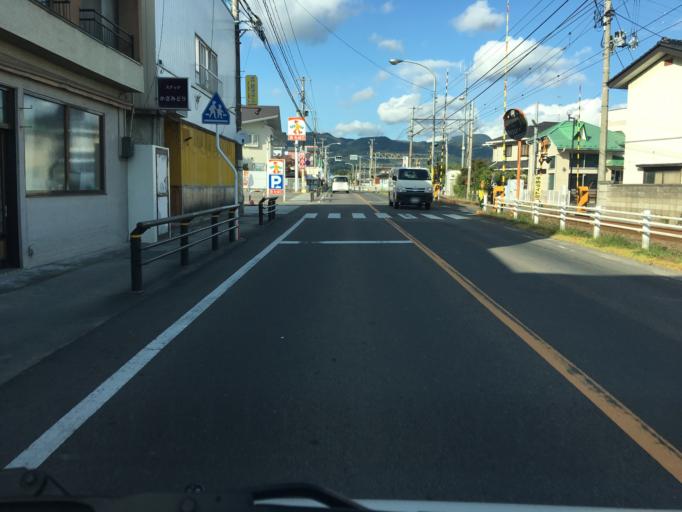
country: JP
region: Fukushima
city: Fukushima-shi
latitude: 37.8153
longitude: 140.4458
